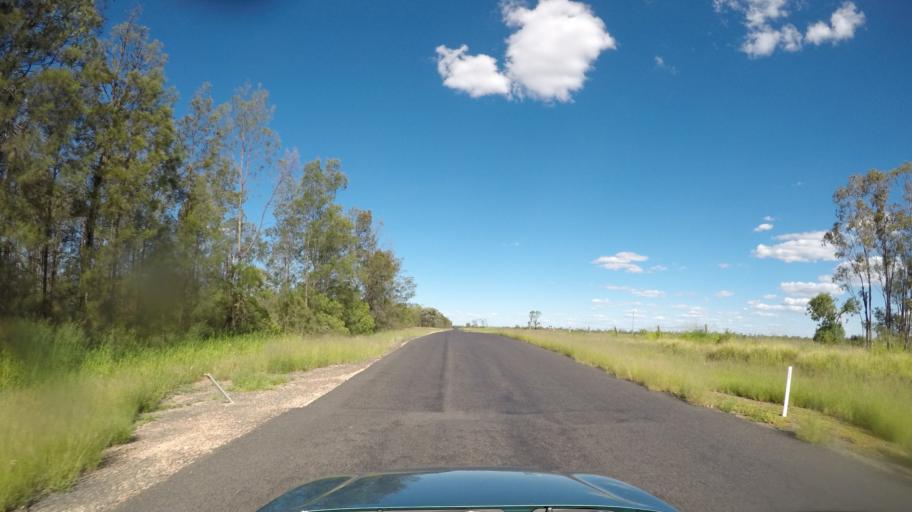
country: AU
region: Queensland
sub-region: Goondiwindi
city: Goondiwindi
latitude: -28.1681
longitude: 150.4548
